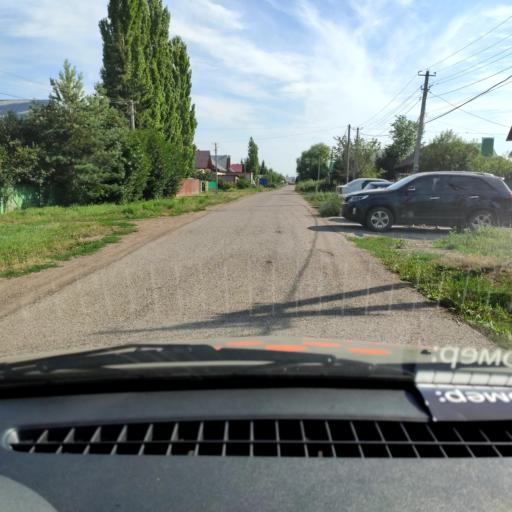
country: RU
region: Bashkortostan
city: Ufa
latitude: 54.6111
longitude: 55.8949
